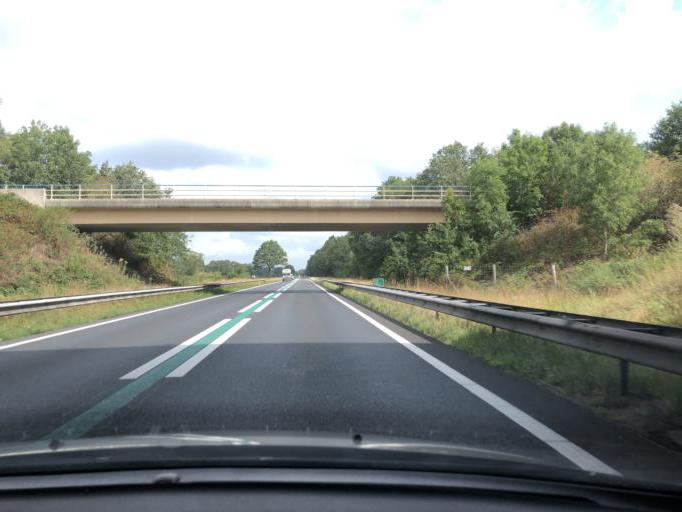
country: NL
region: Drenthe
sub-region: Gemeente Hoogeveen
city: Hoogeveen
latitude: 52.6439
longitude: 6.4357
